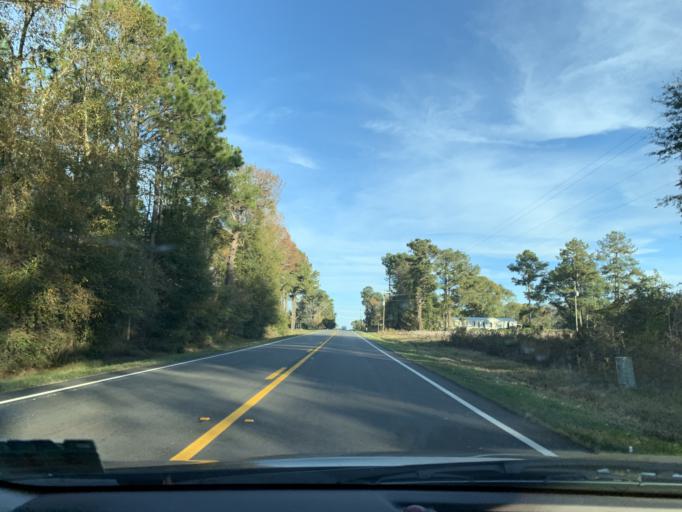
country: US
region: Georgia
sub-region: Irwin County
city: Ocilla
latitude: 31.5956
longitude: -83.1334
